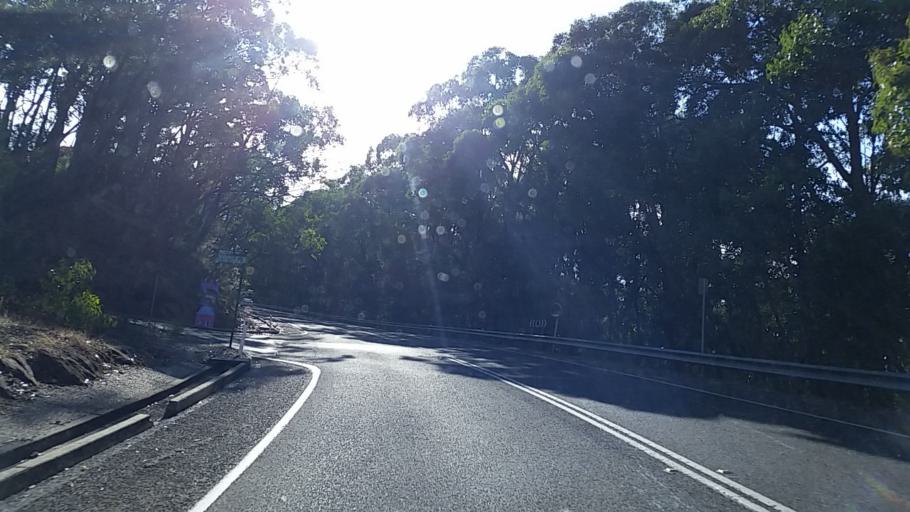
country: AU
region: South Australia
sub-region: Adelaide Hills
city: Crafers
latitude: -34.9954
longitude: 138.7065
